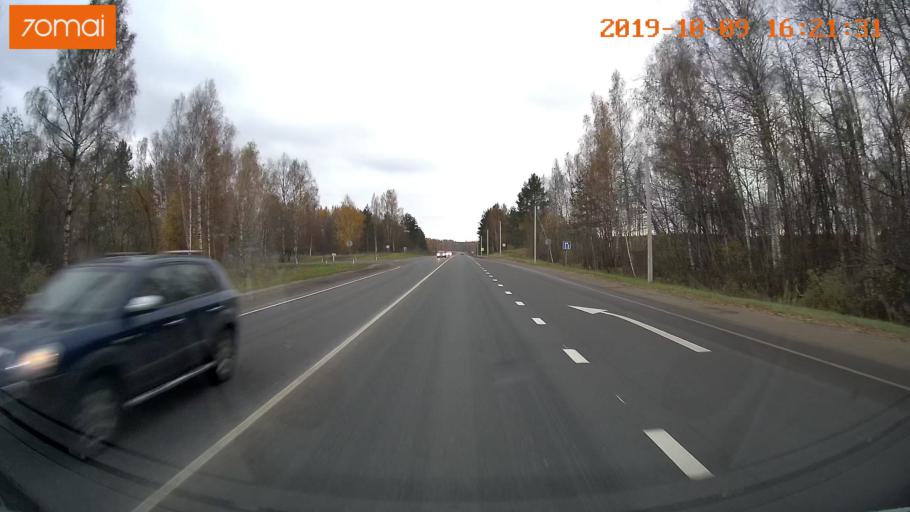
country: RU
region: Kostroma
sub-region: Kostromskoy Rayon
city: Kostroma
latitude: 57.6907
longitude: 40.8889
